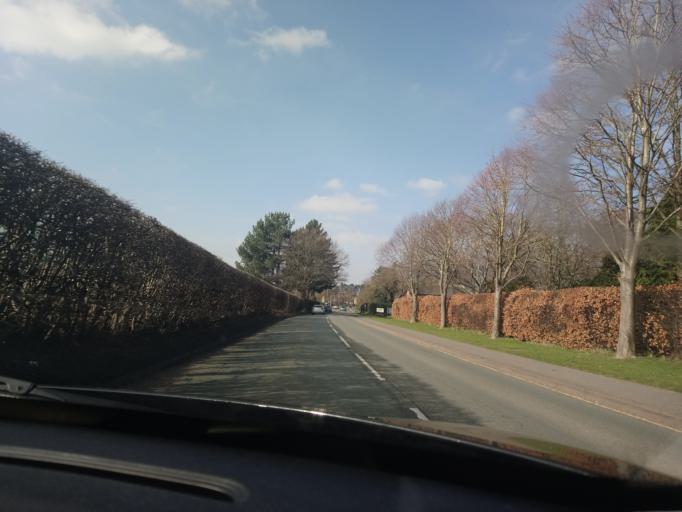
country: GB
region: England
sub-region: Shropshire
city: Shrewsbury
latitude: 52.6950
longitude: -2.7207
